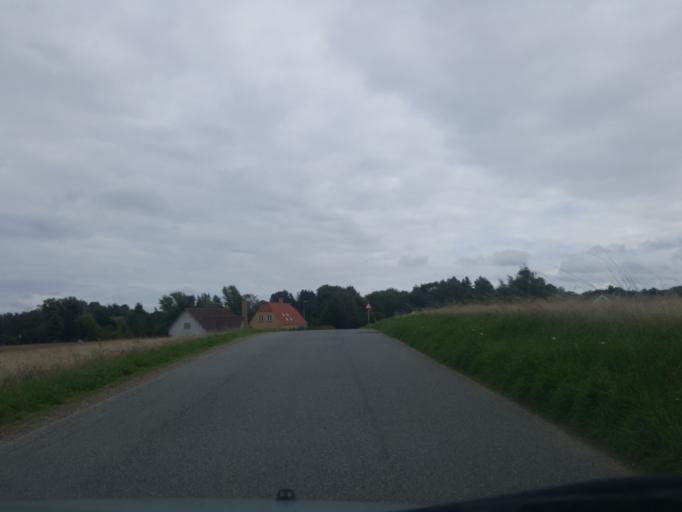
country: DK
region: Zealand
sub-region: Soro Kommune
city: Soro
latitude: 55.4467
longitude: 11.5294
